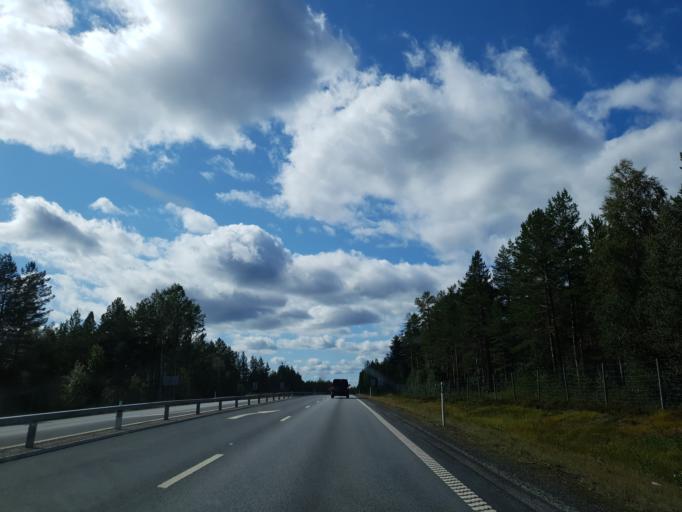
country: SE
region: Vaesterbotten
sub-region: Umea Kommun
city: Hoernefors
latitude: 63.6047
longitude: 19.7662
